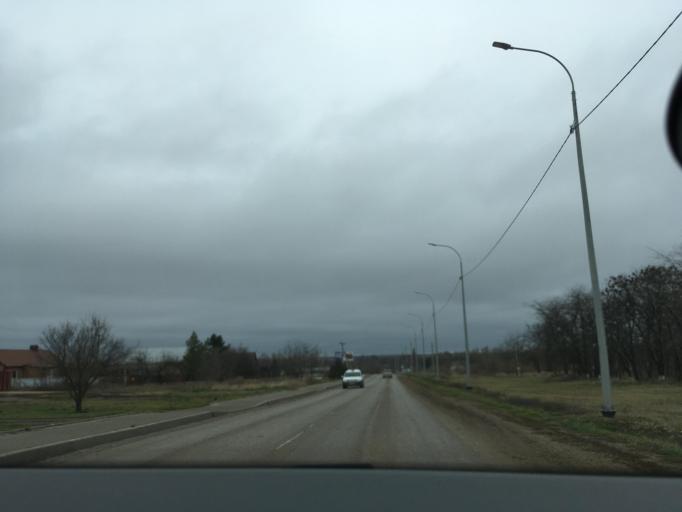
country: RU
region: Krasnodarskiy
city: Kushchevskaya
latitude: 46.5820
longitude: 39.6395
